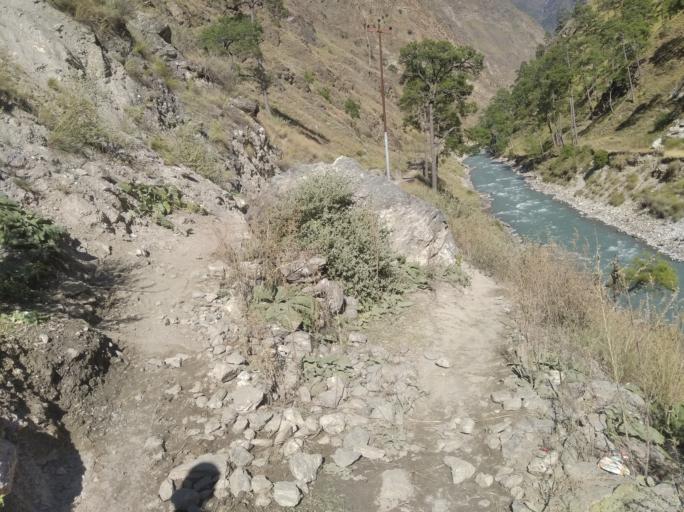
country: NP
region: Mid Western
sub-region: Karnali Zone
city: Jumla
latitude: 28.9335
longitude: 82.9205
